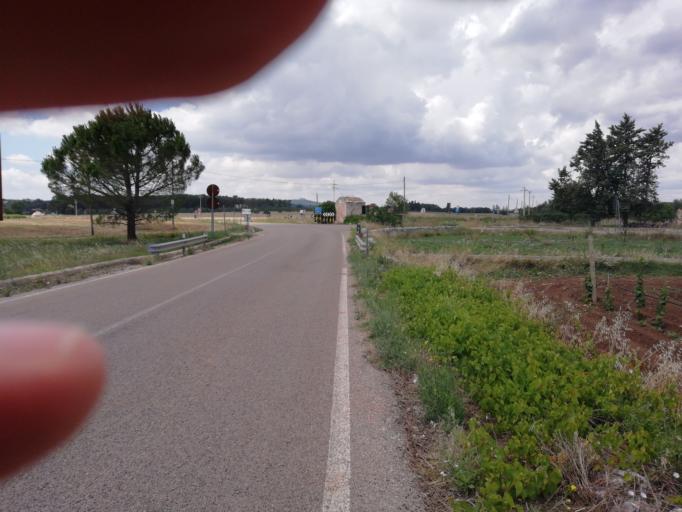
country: IT
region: Apulia
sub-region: Provincia di Bari
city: Corato
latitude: 41.0949
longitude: 16.3386
